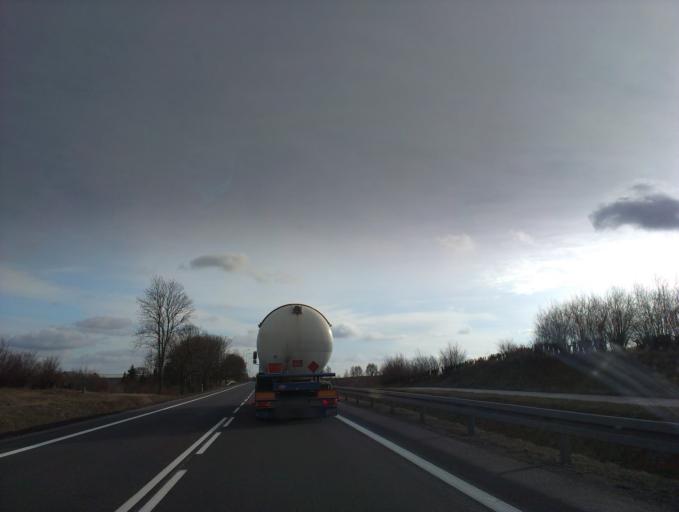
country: PL
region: Kujawsko-Pomorskie
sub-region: Powiat lipnowski
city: Kikol
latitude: 52.8910
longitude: 19.1264
